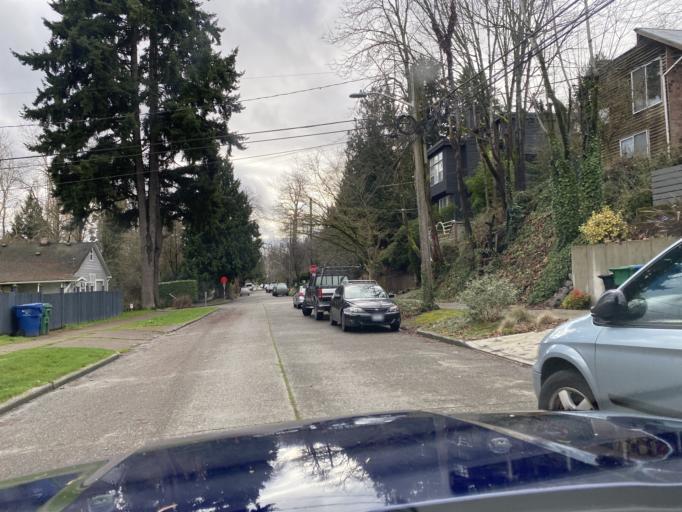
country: US
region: Washington
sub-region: King County
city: Seattle
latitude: 47.6257
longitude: -122.2988
